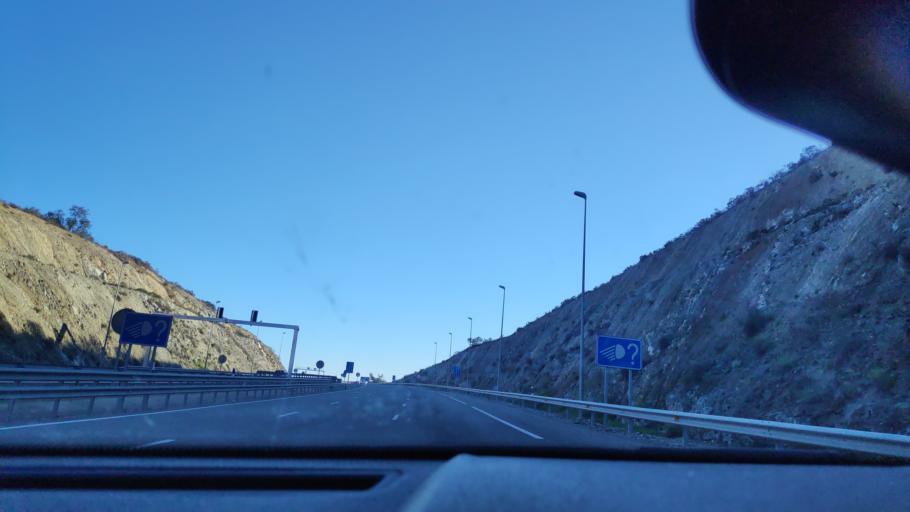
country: ES
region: Andalusia
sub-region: Provincia de Sevilla
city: El Ronquillo
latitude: 37.6408
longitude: -6.1556
